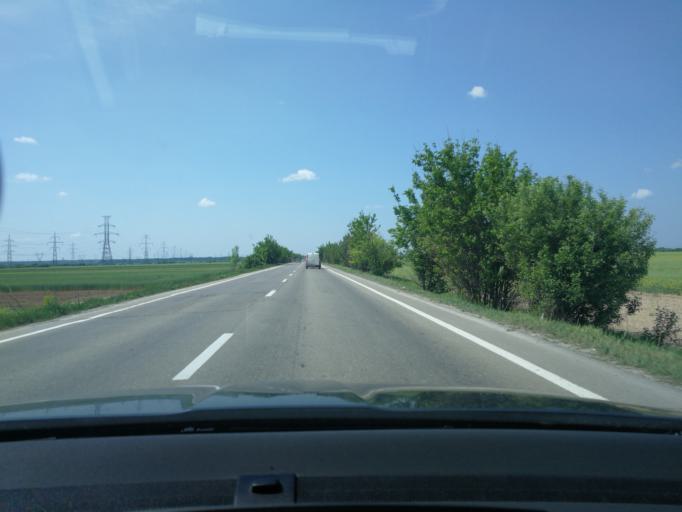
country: RO
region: Prahova
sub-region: Comuna Brazi
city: Negoiesti
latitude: 44.8849
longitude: 25.9521
